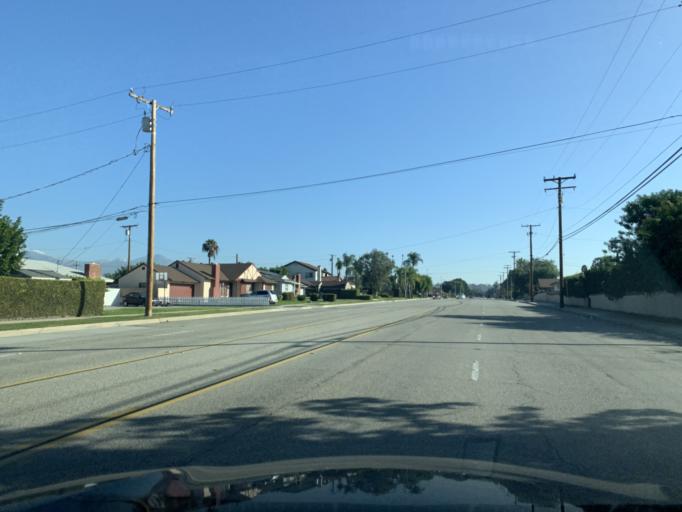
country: US
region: California
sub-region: Los Angeles County
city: Covina
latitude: 34.0790
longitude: -117.8784
